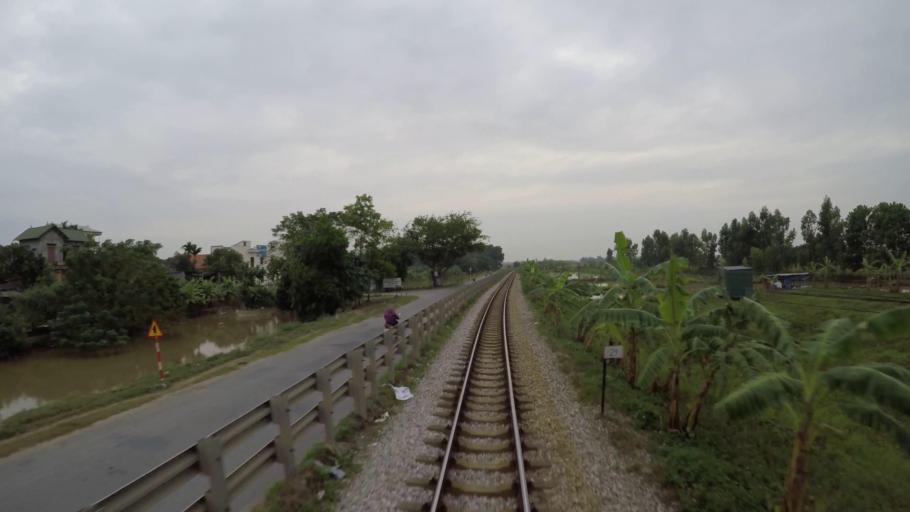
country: VN
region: Hung Yen
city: Ban Yen Nhan
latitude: 20.9830
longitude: 106.0747
